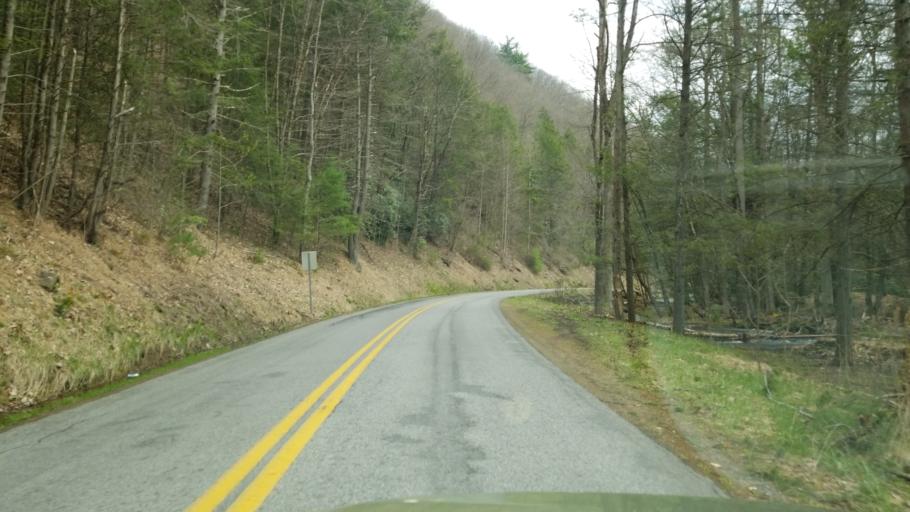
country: US
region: Pennsylvania
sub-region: Cameron County
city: Emporium
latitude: 41.2880
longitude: -78.1232
